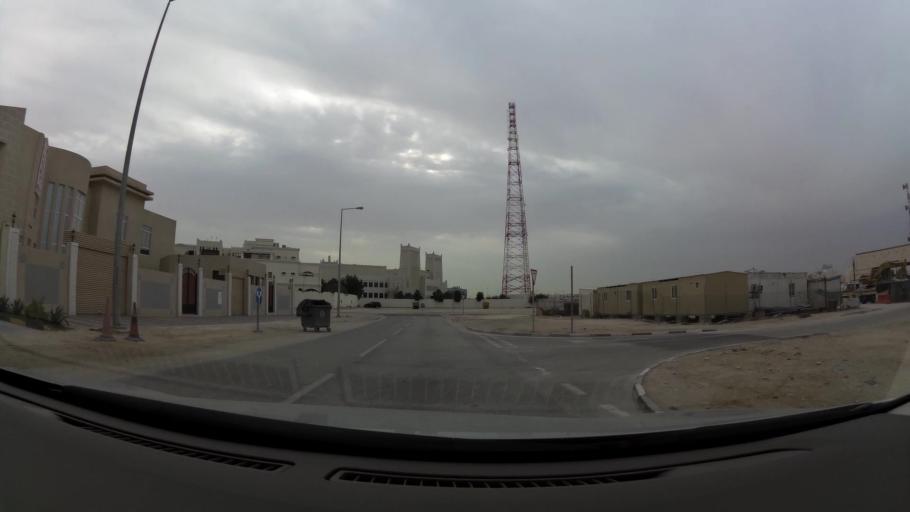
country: QA
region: Baladiyat ad Dawhah
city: Doha
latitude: 25.3100
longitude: 51.5011
